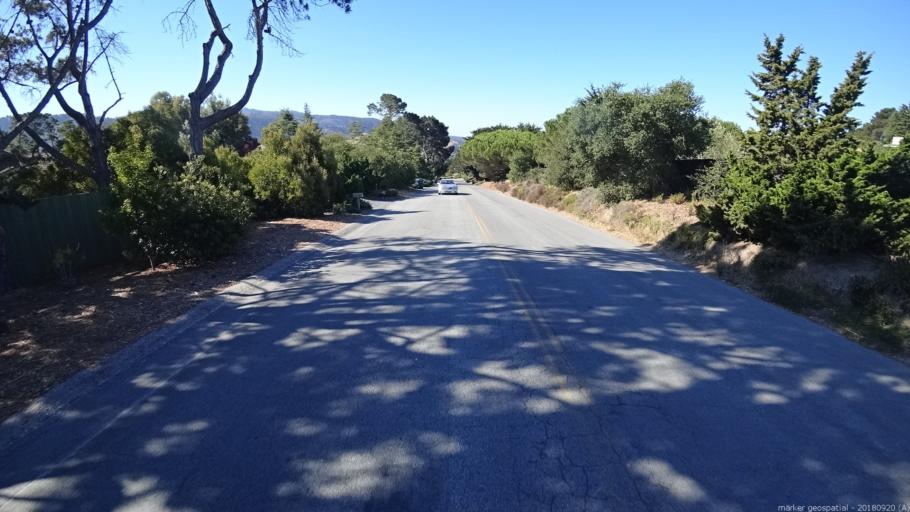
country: US
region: California
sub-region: Monterey County
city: Carmel-by-the-Sea
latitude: 36.5483
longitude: -121.9008
